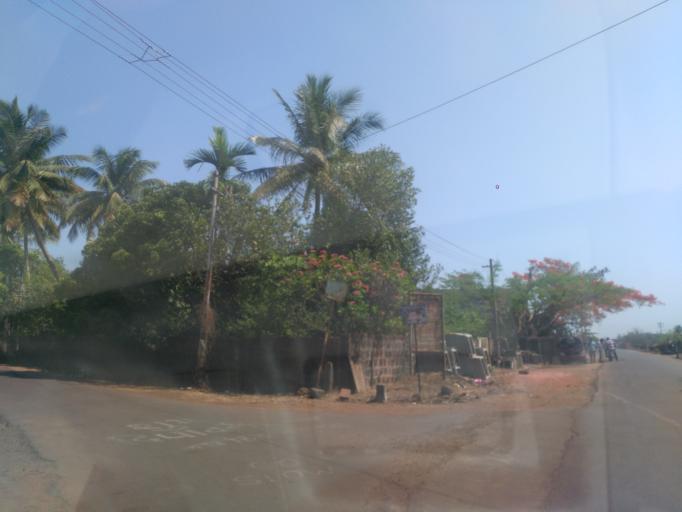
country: IN
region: Maharashtra
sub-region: Ratnagiri
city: Makhjan
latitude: 17.2388
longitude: 73.2710
